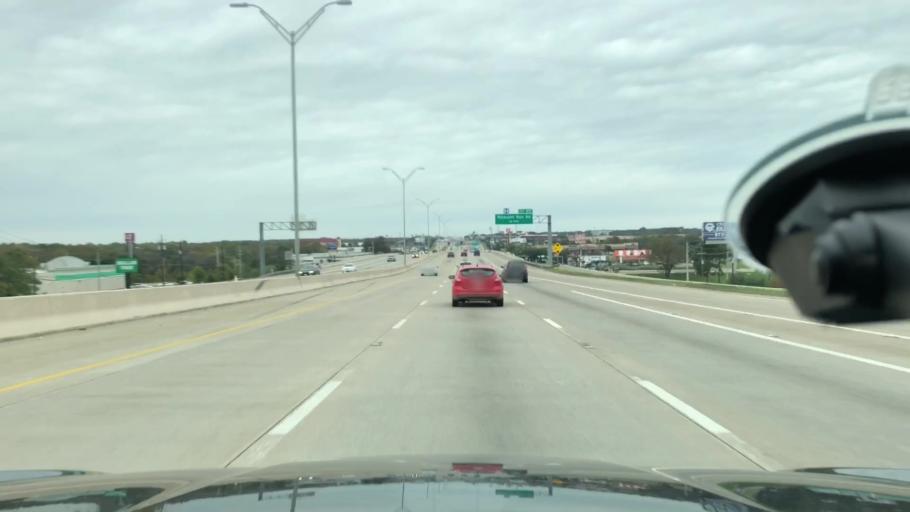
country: US
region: Texas
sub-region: Dallas County
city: DeSoto
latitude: 32.5873
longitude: -96.8223
